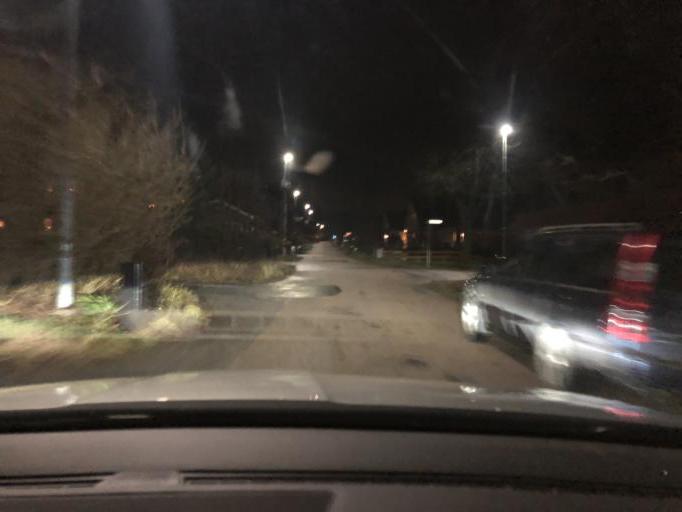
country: SE
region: Stockholm
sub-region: Jarfalla Kommun
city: Jakobsberg
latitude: 59.4661
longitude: 17.8245
